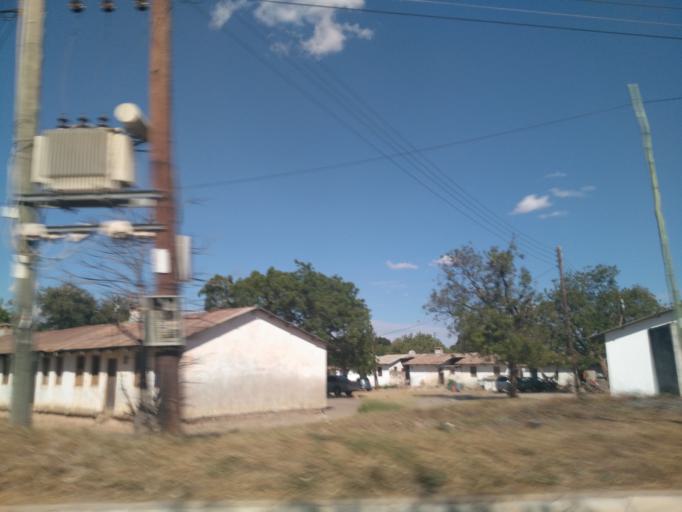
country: TZ
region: Dodoma
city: Dodoma
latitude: -6.1858
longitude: 35.7418
